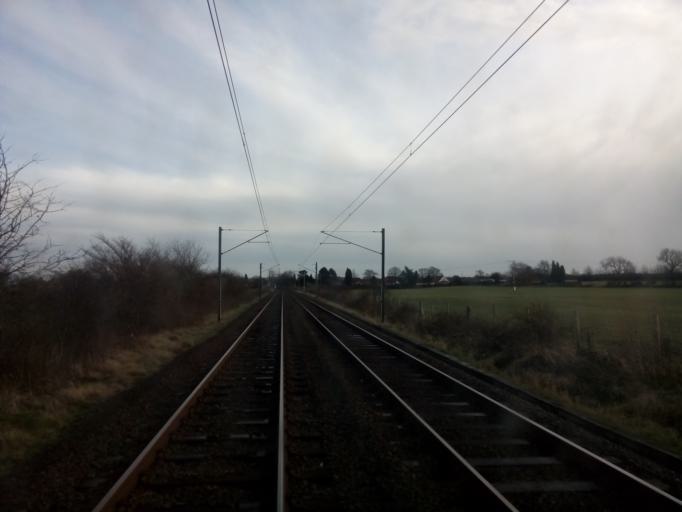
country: GB
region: England
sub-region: Newcastle upon Tyne
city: Dinnington
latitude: 55.0159
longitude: -1.6847
